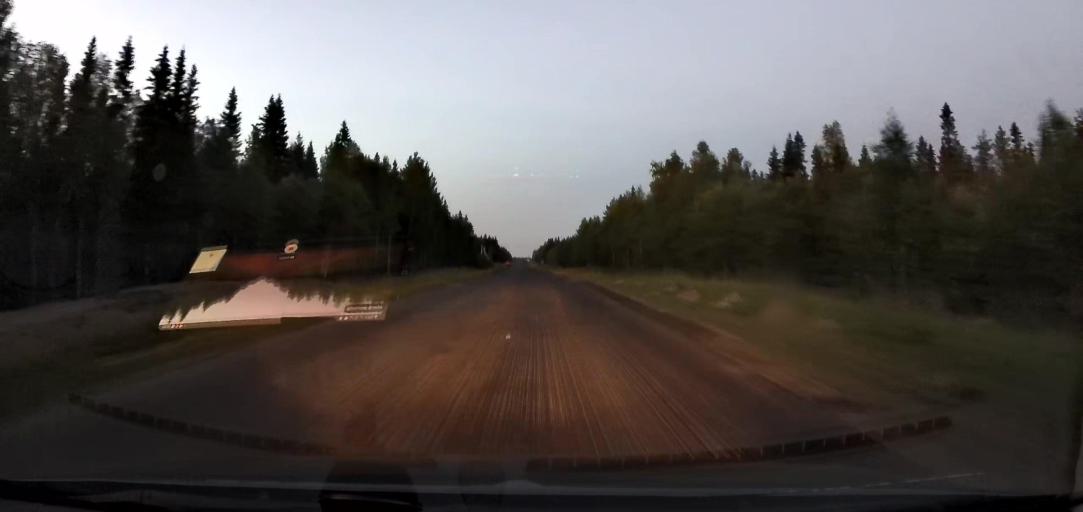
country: RU
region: Arkhangelskaya
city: Kholmogory
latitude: 64.3333
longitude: 41.3944
